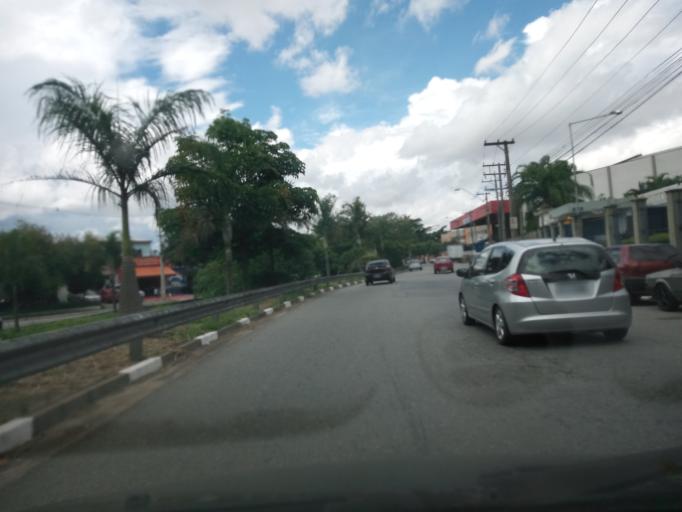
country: BR
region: Sao Paulo
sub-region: Sao Bernardo Do Campo
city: Sao Bernardo do Campo
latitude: -23.6943
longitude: -46.5800
